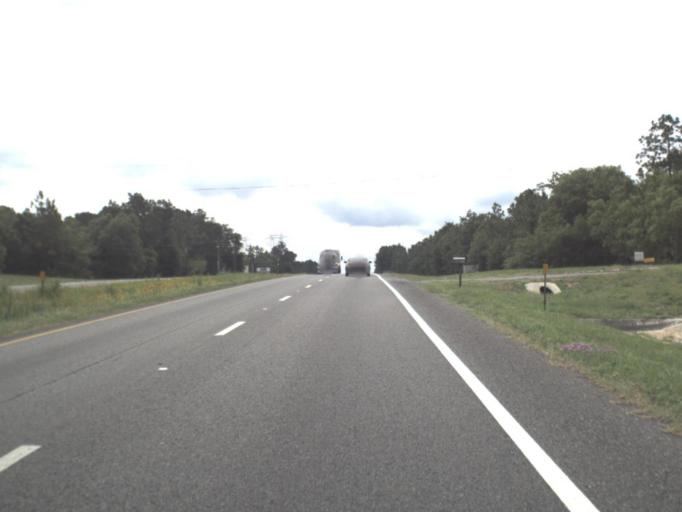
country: US
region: Florida
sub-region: Nassau County
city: Hilliard
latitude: 30.7520
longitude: -81.9605
